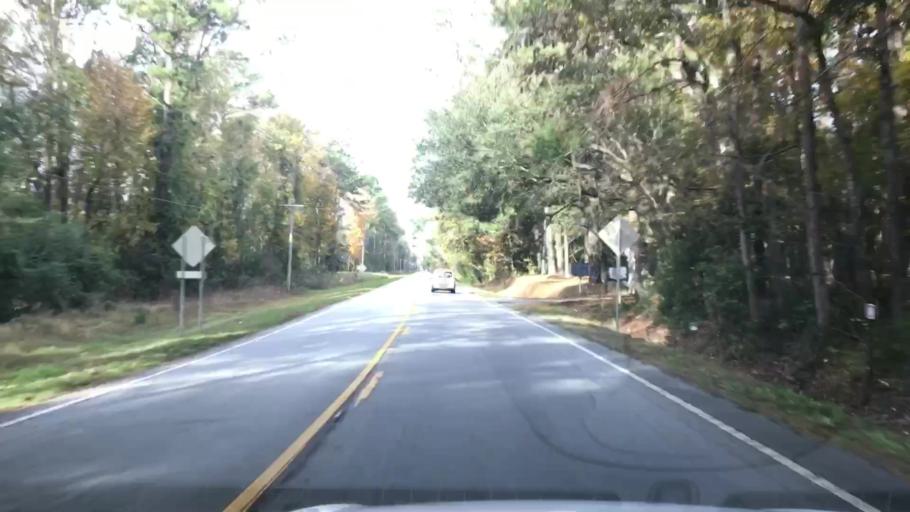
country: US
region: South Carolina
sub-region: Colleton County
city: Walterboro
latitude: 32.7971
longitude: -80.4905
